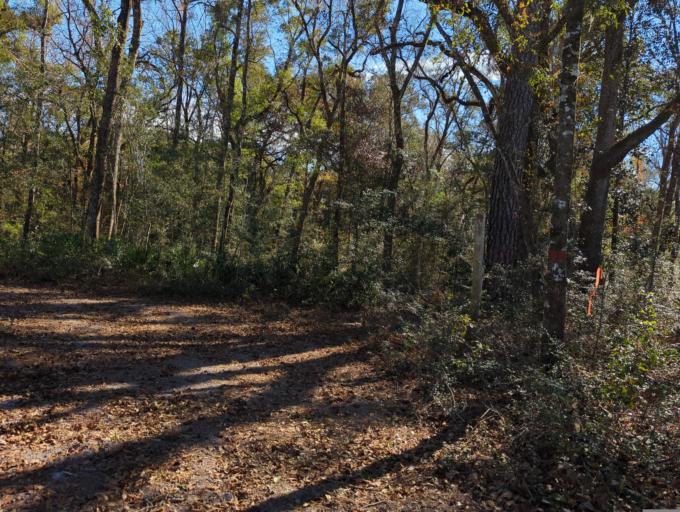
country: US
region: Florida
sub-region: Wakulla County
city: Crawfordville
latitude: 30.1823
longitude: -84.3322
